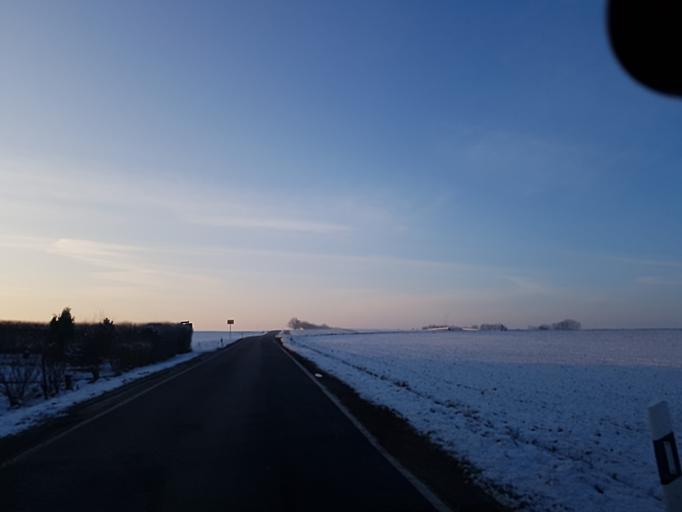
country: DE
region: Saxony
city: Mugeln
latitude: 51.2039
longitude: 13.0307
